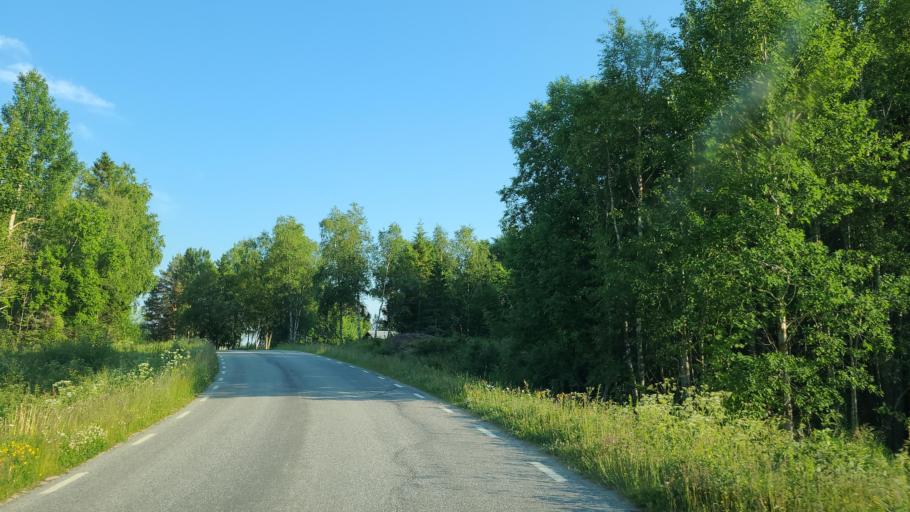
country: SE
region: Vaesterbotten
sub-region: Skelleftea Kommun
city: Burea
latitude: 64.3460
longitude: 21.3398
